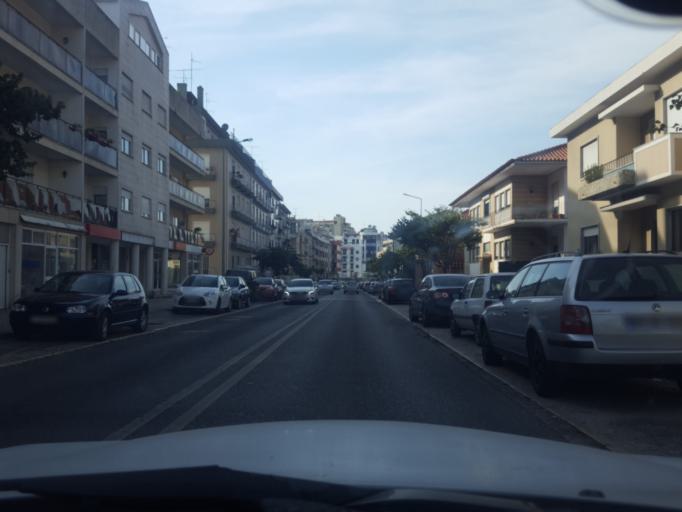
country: PT
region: Leiria
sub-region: Leiria
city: Leiria
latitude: 39.7377
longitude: -8.8006
